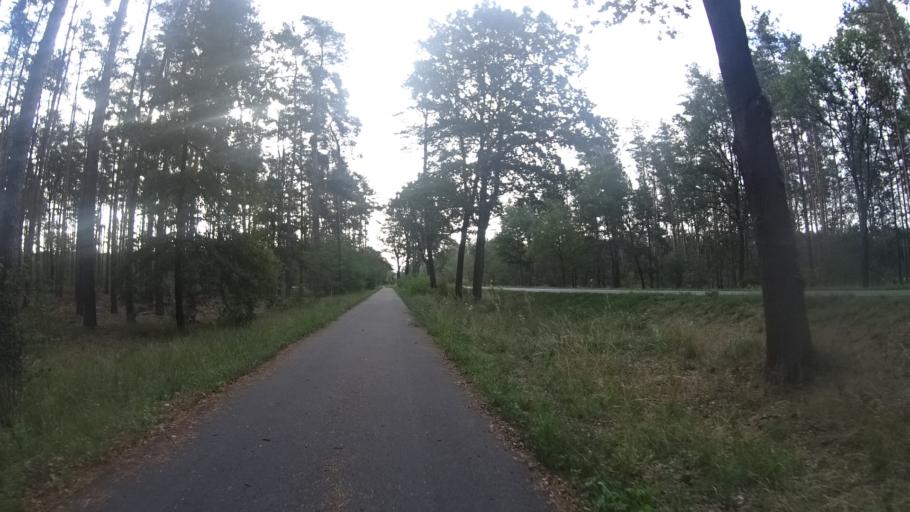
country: DE
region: Brandenburg
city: Premnitz
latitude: 52.5140
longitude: 12.4197
